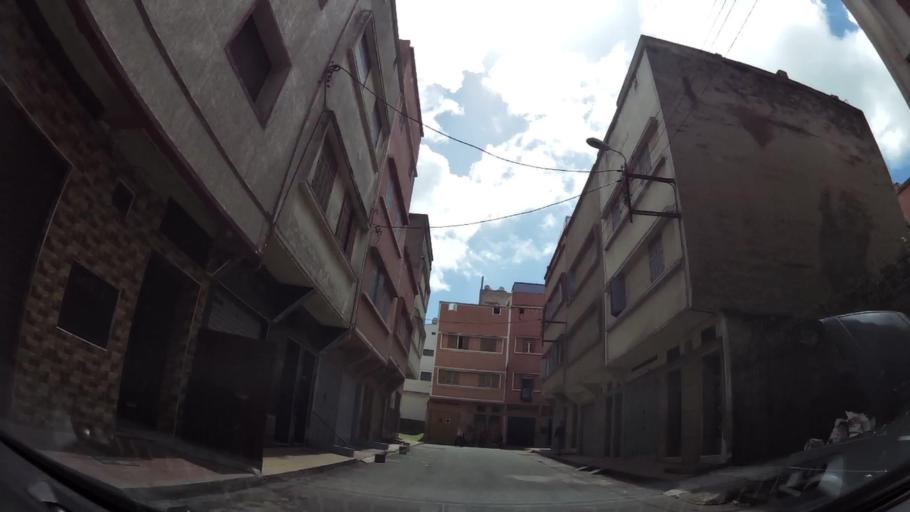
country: MA
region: Grand Casablanca
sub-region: Casablanca
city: Casablanca
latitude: 33.5383
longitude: -7.5859
